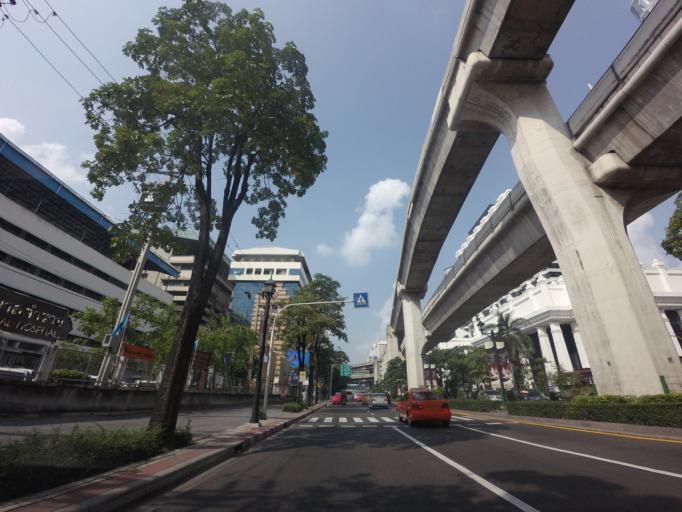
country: TH
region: Bangkok
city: Pathum Wan
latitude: 13.7425
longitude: 100.5398
